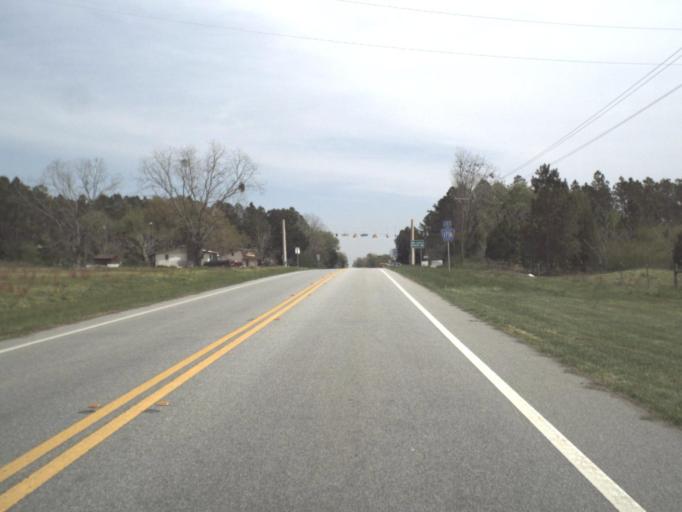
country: US
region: Alabama
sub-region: Geneva County
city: Geneva
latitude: 30.9456
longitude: -85.7646
